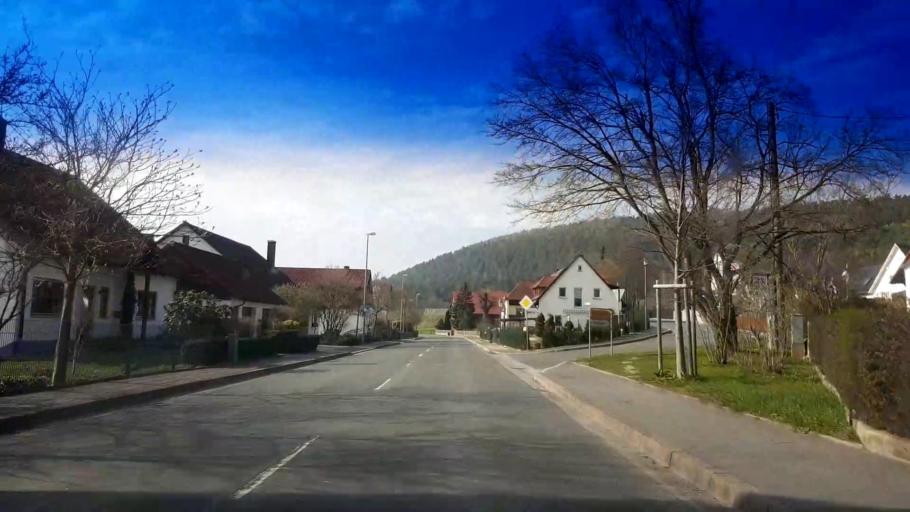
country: DE
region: Bavaria
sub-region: Upper Franconia
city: Harsdorf
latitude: 50.0300
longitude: 11.5646
